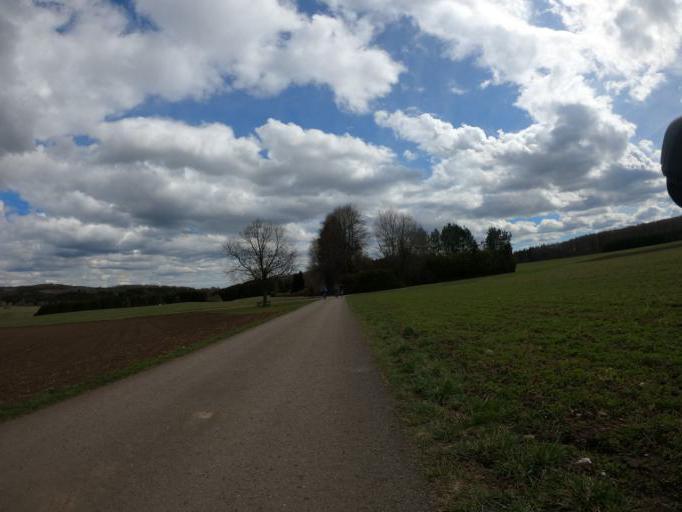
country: DE
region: Baden-Wuerttemberg
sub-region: Tuebingen Region
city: Trochtelfingen
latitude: 48.3779
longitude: 9.2057
